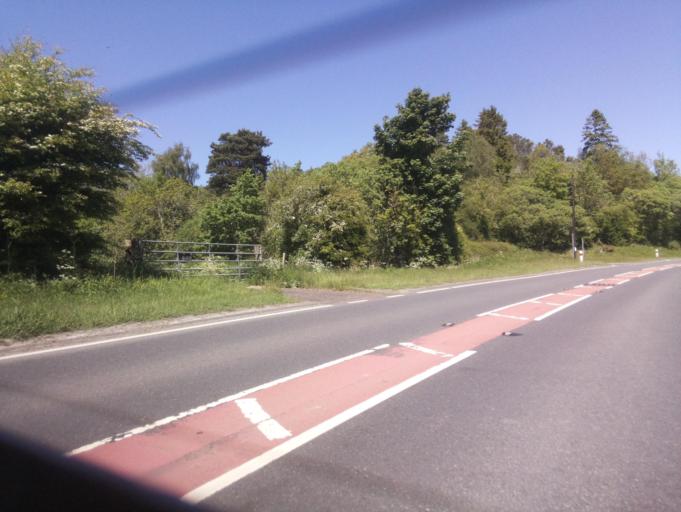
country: GB
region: Scotland
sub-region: The Scottish Borders
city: Hawick
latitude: 55.3833
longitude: -2.8690
